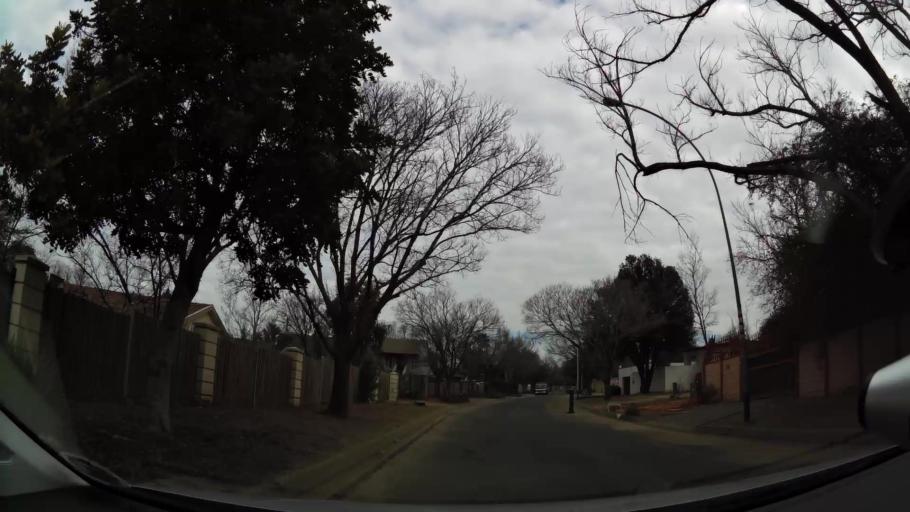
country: ZA
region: Orange Free State
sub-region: Mangaung Metropolitan Municipality
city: Bloemfontein
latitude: -29.0943
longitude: 26.2133
